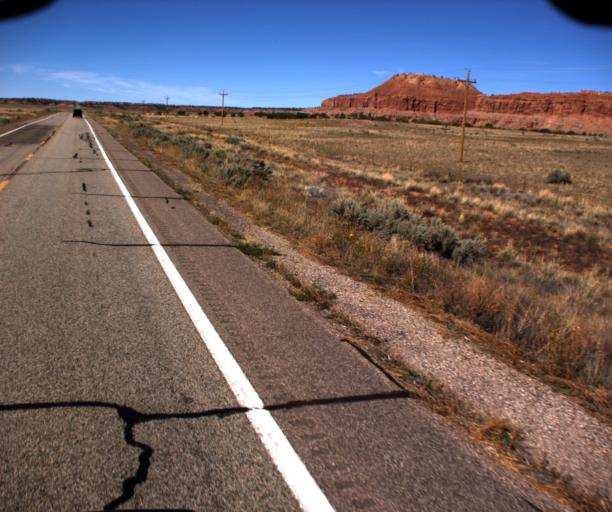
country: US
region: Arizona
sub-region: Mohave County
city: Colorado City
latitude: 36.8693
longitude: -112.8502
